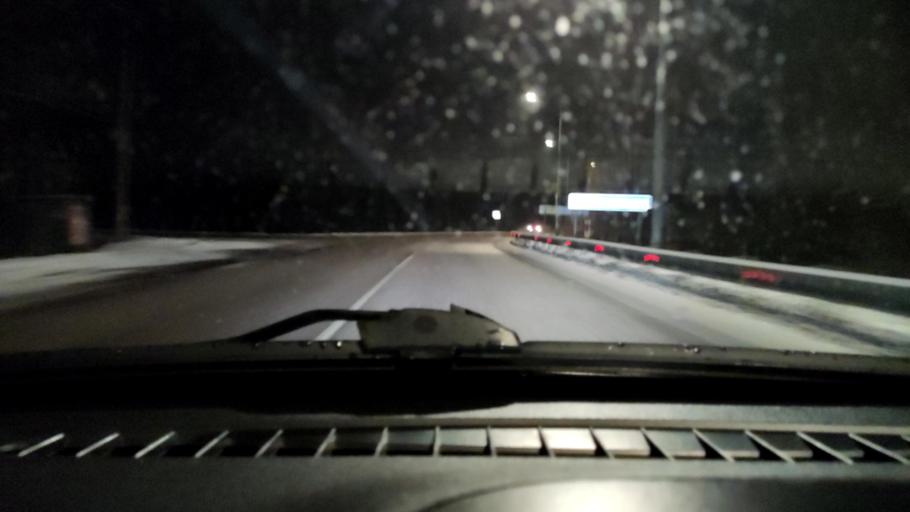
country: RU
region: Voronezj
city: Ramon'
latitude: 51.8913
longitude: 39.2198
